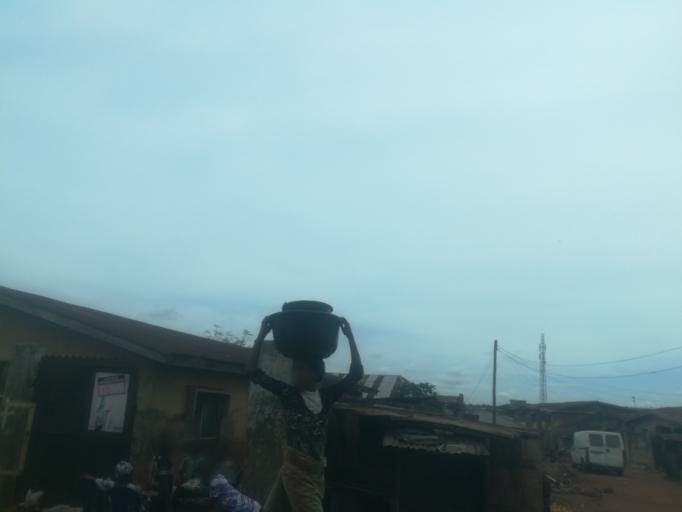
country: NG
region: Oyo
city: Ibadan
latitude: 7.3784
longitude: 3.9474
